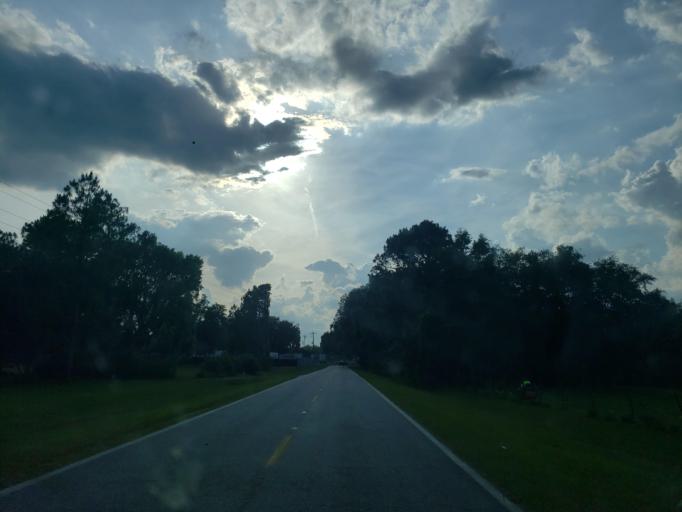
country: US
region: Georgia
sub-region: Echols County
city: Statenville
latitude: 30.6637
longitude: -83.2053
